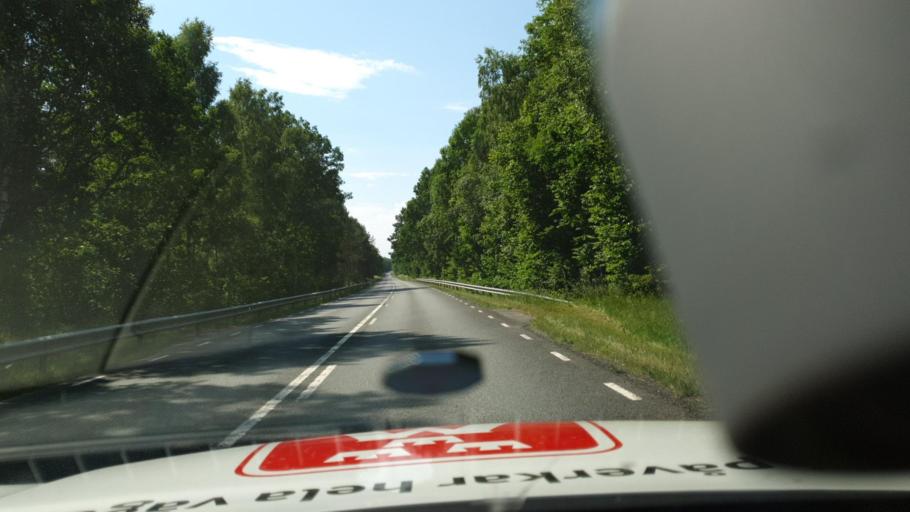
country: SE
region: Vaestra Goetaland
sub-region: Hjo Kommun
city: Hjo
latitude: 58.1111
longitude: 14.2086
